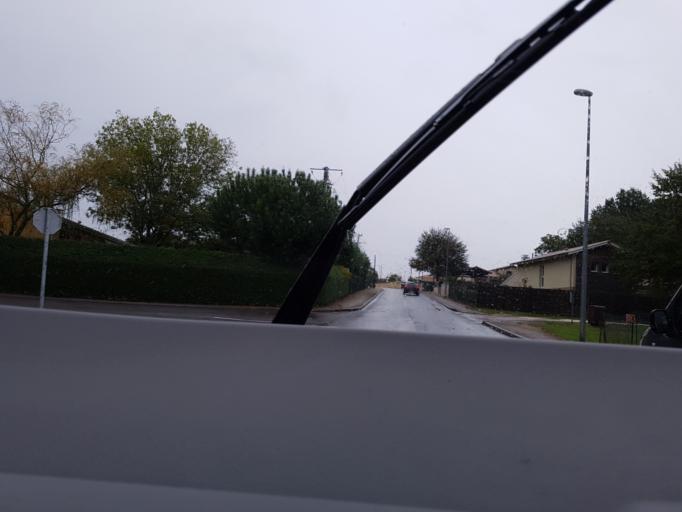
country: FR
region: Aquitaine
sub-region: Departement de la Gironde
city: Saint-Savin
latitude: 45.1360
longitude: -0.4434
